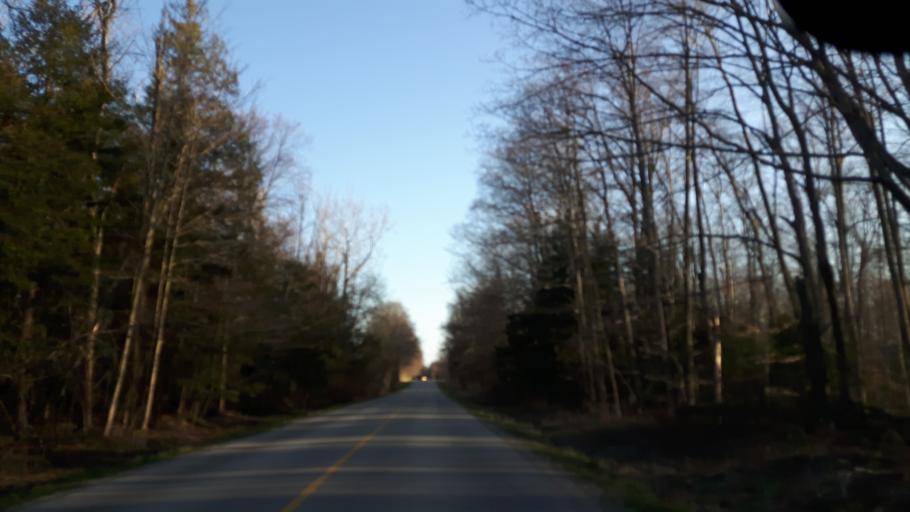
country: CA
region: Ontario
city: Goderich
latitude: 43.6192
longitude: -81.6847
